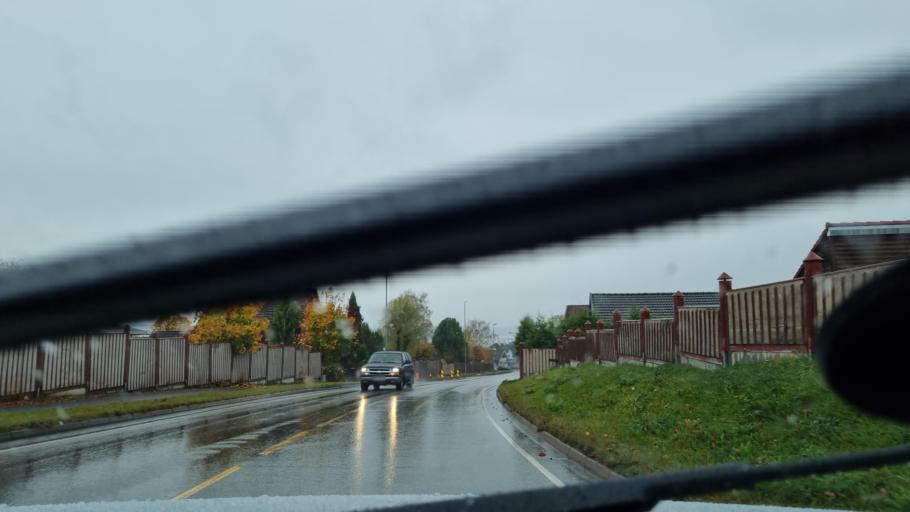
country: NO
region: Hedmark
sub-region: Hamar
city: Hamar
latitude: 60.8110
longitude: 11.0598
